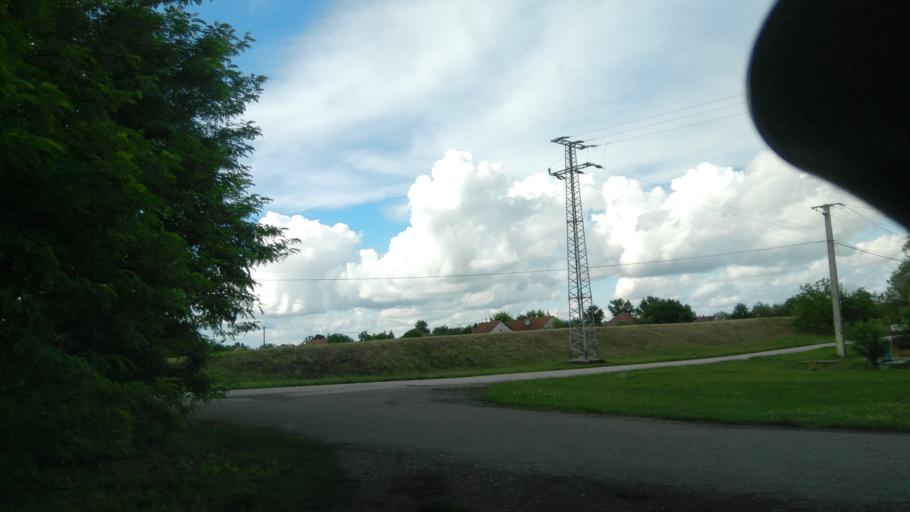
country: HU
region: Bekes
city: Doboz
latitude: 46.7006
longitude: 21.1801
